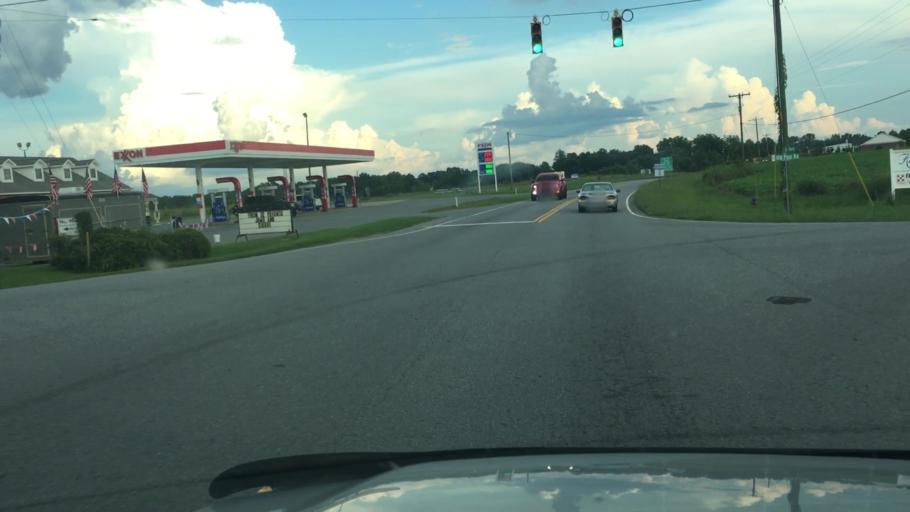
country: US
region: South Carolina
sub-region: Cherokee County
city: Gaffney
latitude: 35.1117
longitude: -81.7006
